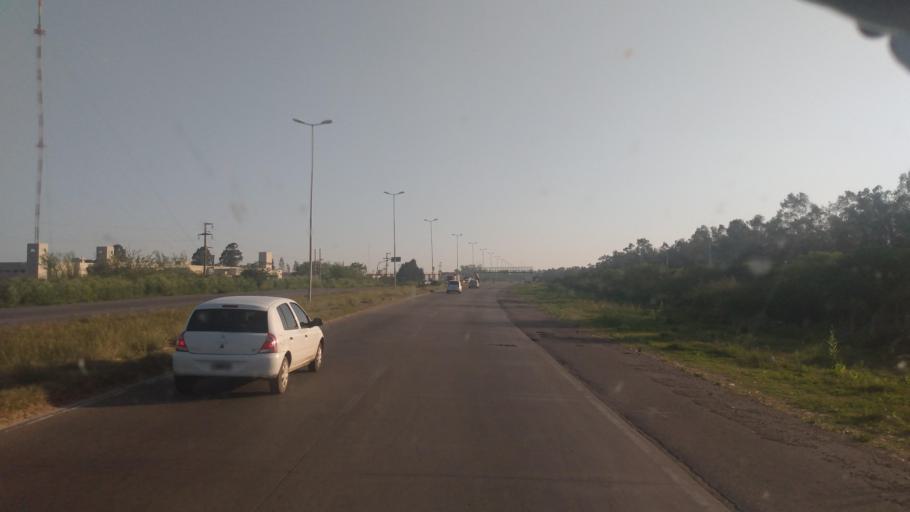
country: AR
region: Buenos Aires
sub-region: Partido de Campana
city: Campana
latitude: -34.2335
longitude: -58.9612
